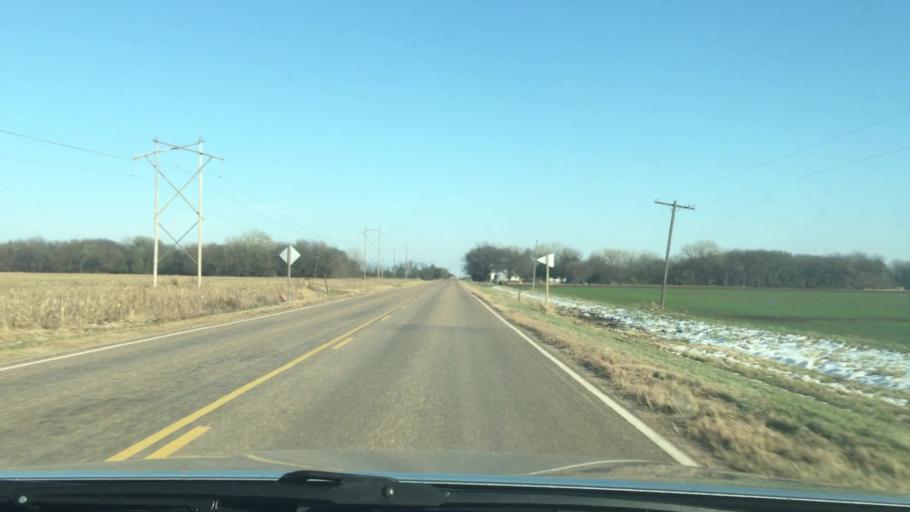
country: US
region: Kansas
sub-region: Rice County
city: Lyons
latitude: 38.2895
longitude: -98.1262
